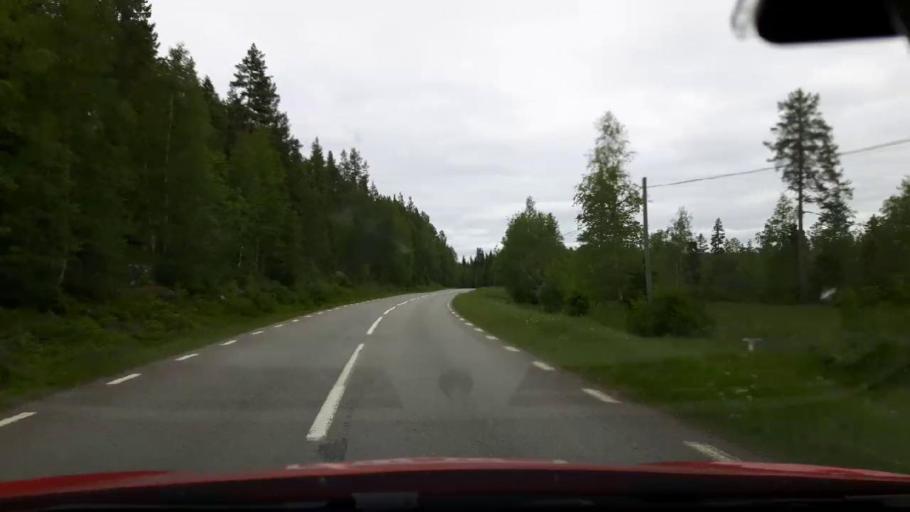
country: SE
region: Jaemtland
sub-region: Stroemsunds Kommun
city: Stroemsund
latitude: 63.4068
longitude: 15.6203
